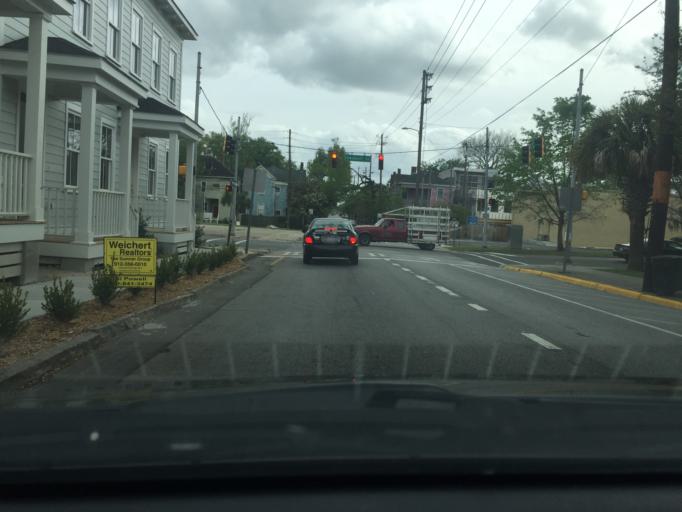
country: US
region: Georgia
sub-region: Chatham County
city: Savannah
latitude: 32.0662
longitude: -81.0910
